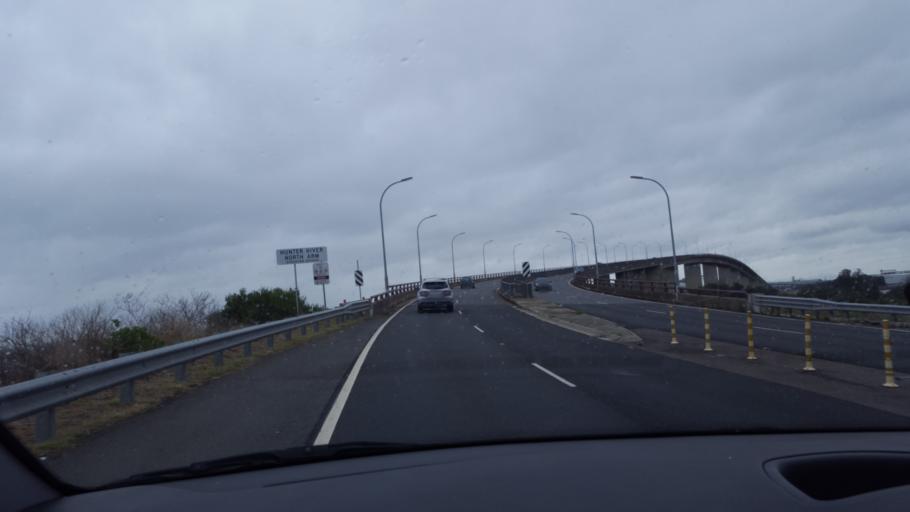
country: AU
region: New South Wales
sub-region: Newcastle
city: Carrington
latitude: -32.8839
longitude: 151.7923
